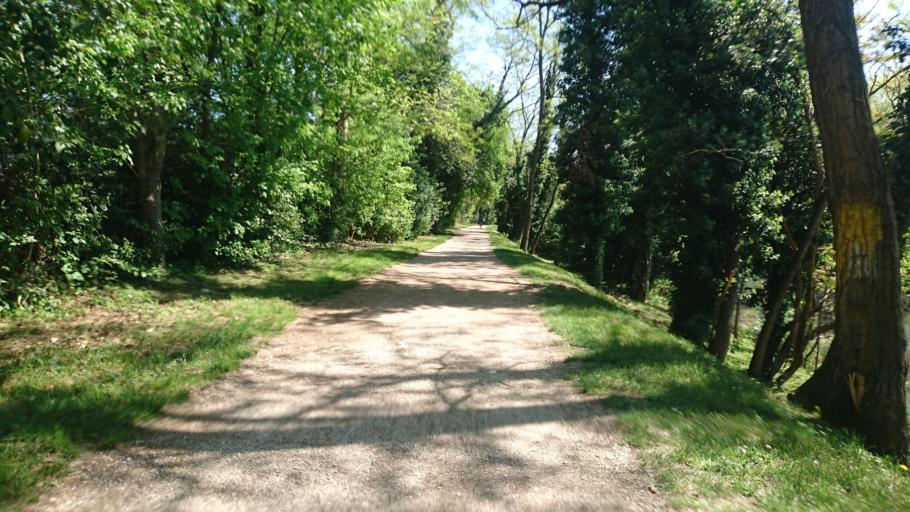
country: IT
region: Veneto
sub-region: Provincia di Treviso
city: Casier
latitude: 45.6447
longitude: 12.2766
